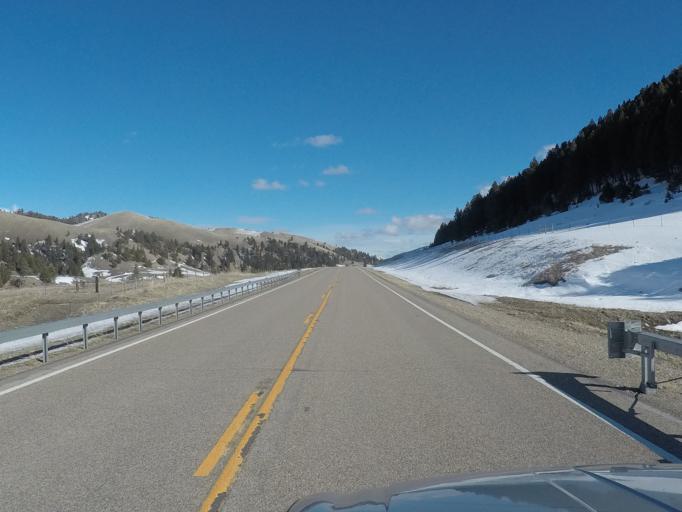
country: US
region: Montana
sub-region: Meagher County
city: White Sulphur Springs
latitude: 46.5651
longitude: -110.5208
